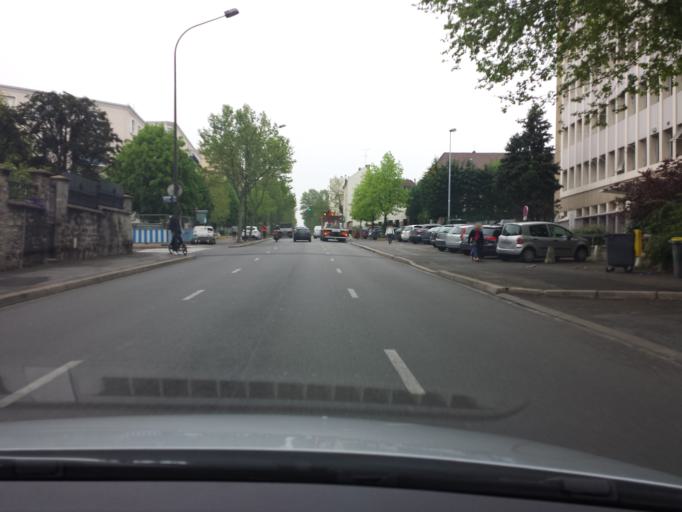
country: FR
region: Ile-de-France
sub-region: Departement des Hauts-de-Seine
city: Bourg-la-Reine
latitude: 48.7828
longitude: 2.3169
